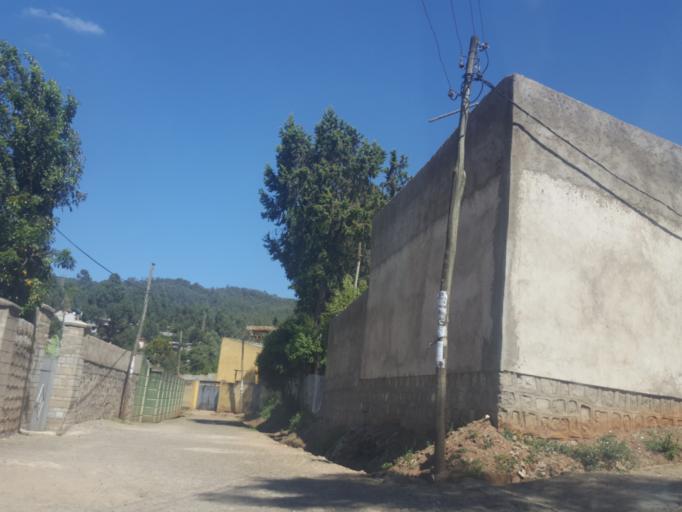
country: ET
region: Adis Abeba
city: Addis Ababa
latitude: 9.0686
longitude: 38.7341
